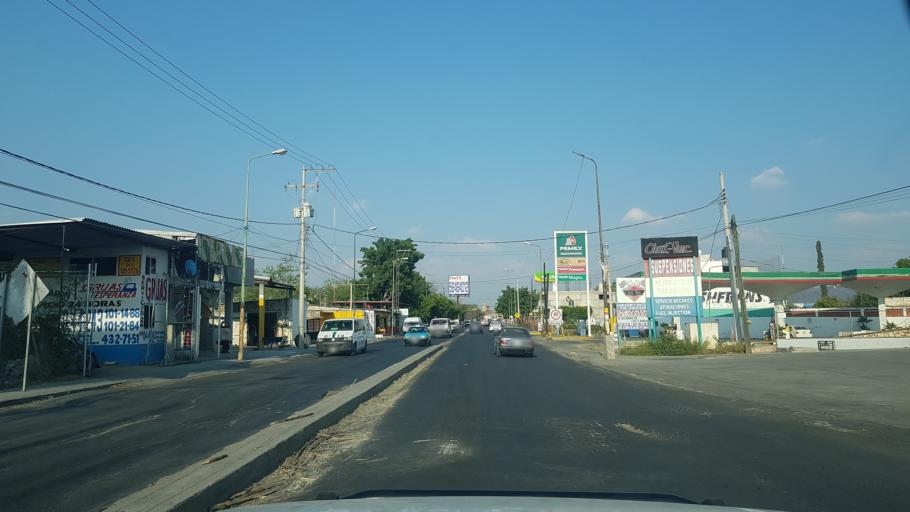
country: MX
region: Puebla
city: Izucar de Matamoros
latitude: 18.6005
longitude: -98.4779
